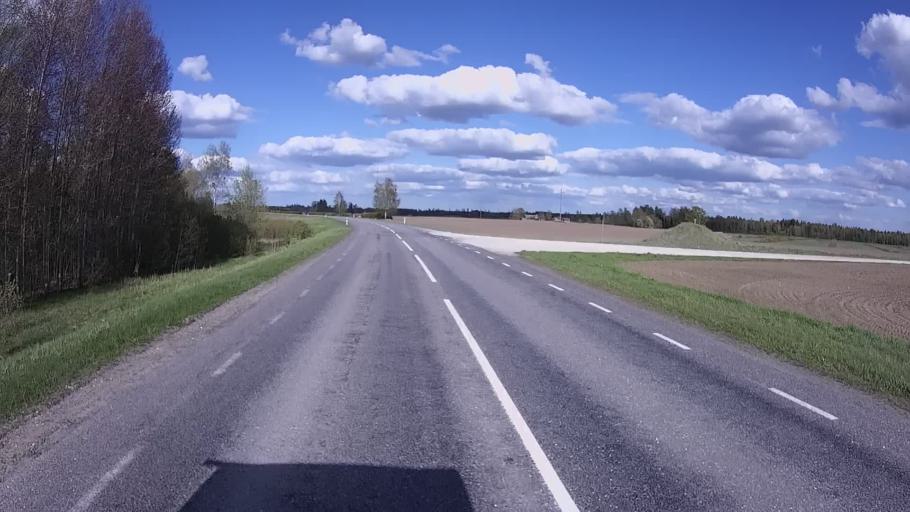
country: EE
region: Jogevamaa
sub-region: Poltsamaa linn
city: Poltsamaa
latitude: 58.6882
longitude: 26.1223
